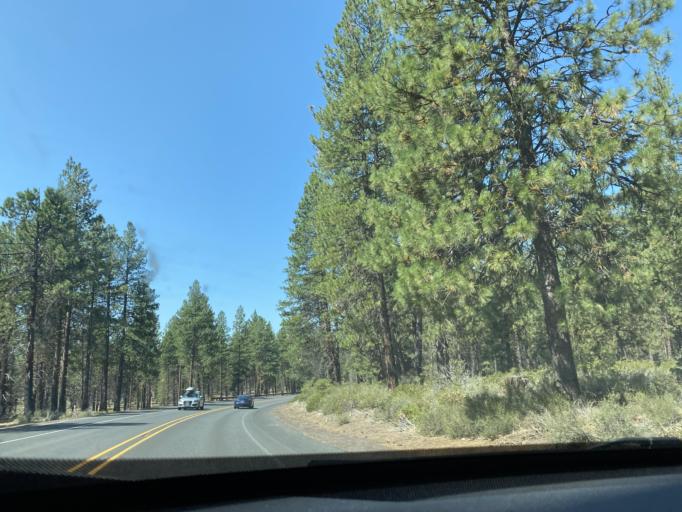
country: US
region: Oregon
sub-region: Deschutes County
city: Sunriver
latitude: 43.8698
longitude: -121.4128
